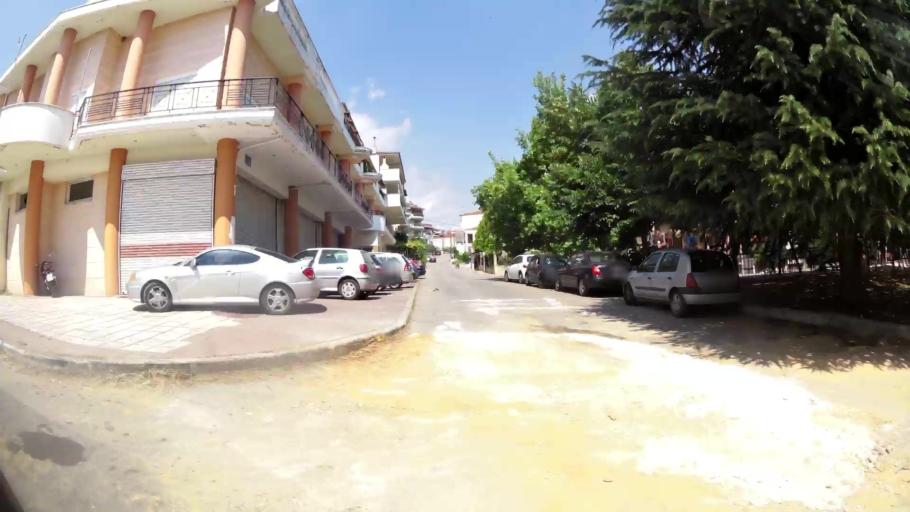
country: GR
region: Central Macedonia
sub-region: Nomos Imathias
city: Veroia
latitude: 40.5099
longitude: 22.2156
